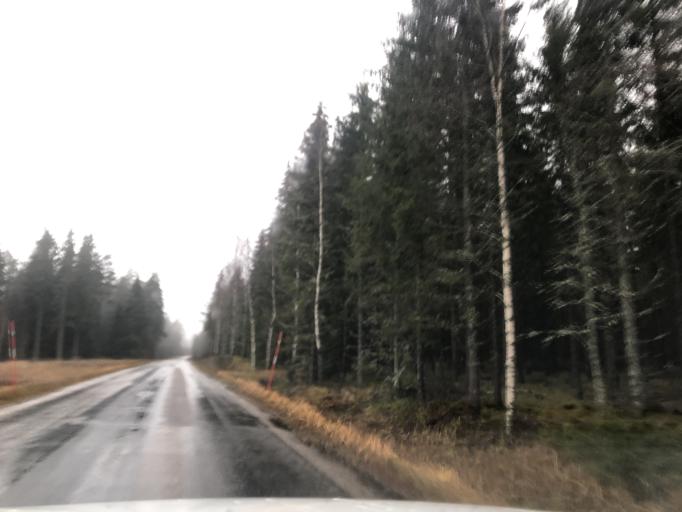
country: SE
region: Vaestra Goetaland
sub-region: Ulricehamns Kommun
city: Ulricehamn
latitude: 57.8394
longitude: 13.5358
